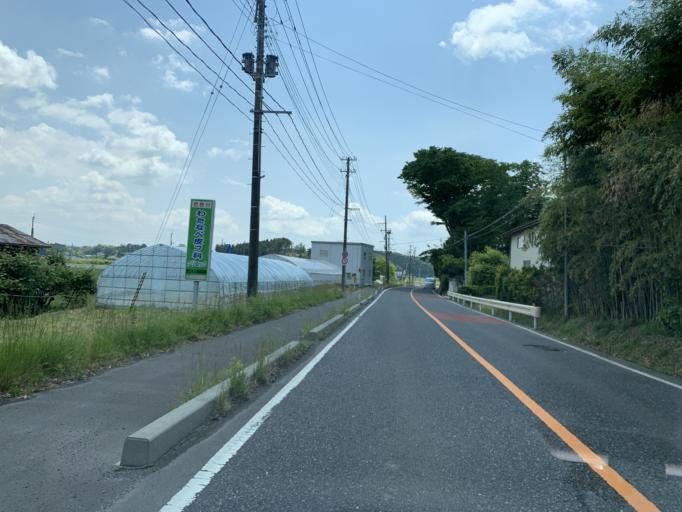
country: JP
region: Miyagi
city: Kogota
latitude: 38.5020
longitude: 141.0800
